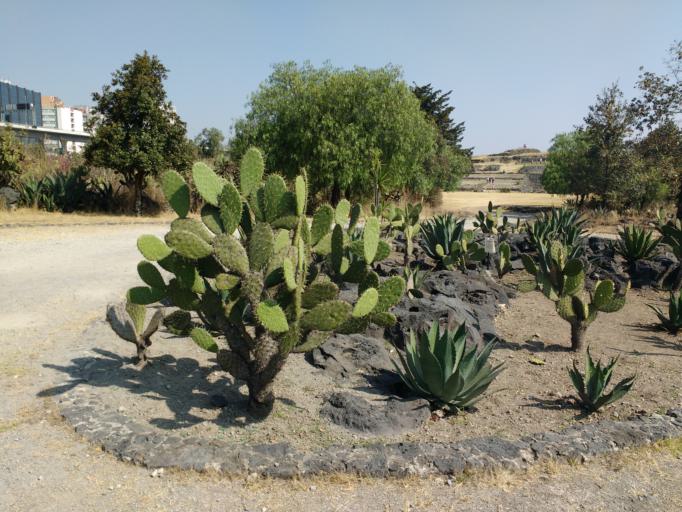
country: MX
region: Mexico City
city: Tlalpan
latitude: 19.3014
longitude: -99.1835
